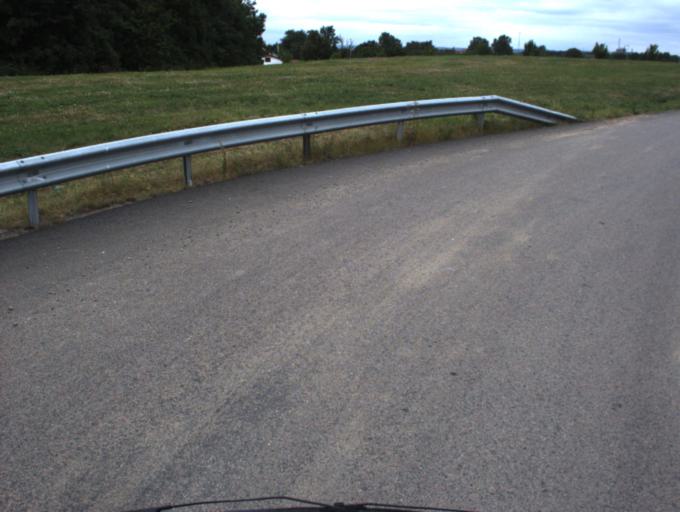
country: SE
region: Skane
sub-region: Helsingborg
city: Rydeback
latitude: 56.0022
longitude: 12.7541
